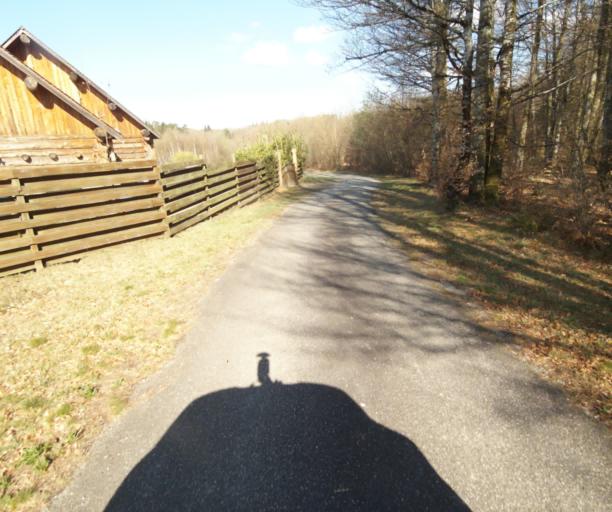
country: FR
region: Limousin
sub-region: Departement de la Correze
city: Laguenne
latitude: 45.2352
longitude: 1.9187
